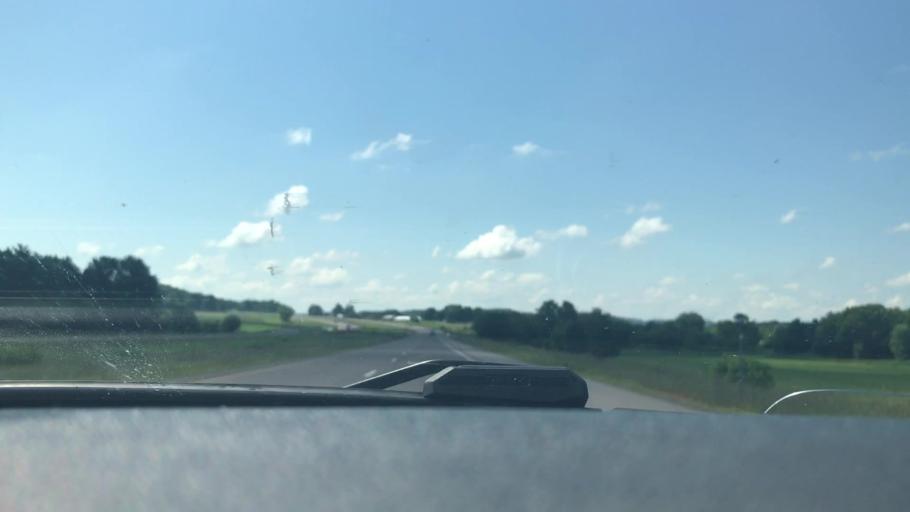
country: US
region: Wisconsin
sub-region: Chippewa County
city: Bloomer
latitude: 45.0548
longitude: -91.4656
